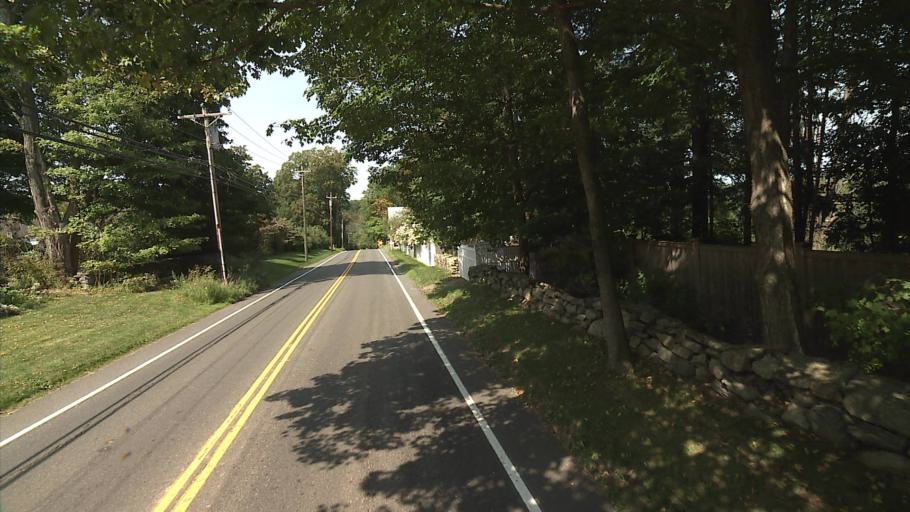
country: US
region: Connecticut
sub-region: Fairfield County
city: Bethel
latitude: 41.3196
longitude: -73.3544
